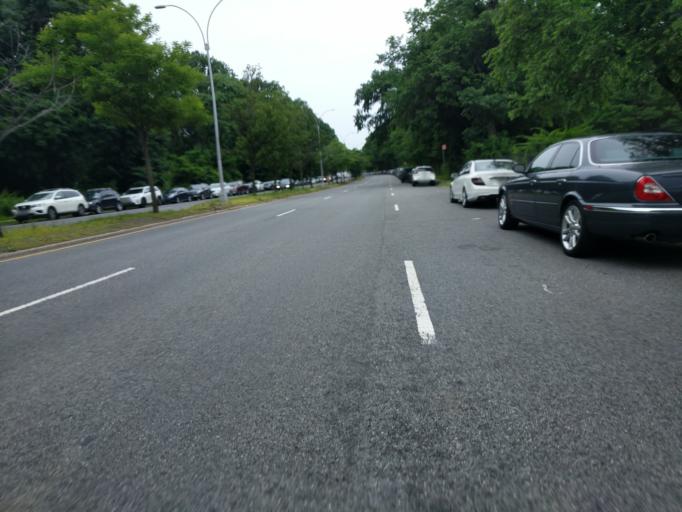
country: US
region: New York
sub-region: Nassau County
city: Bellerose Terrace
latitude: 40.7386
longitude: -73.7737
